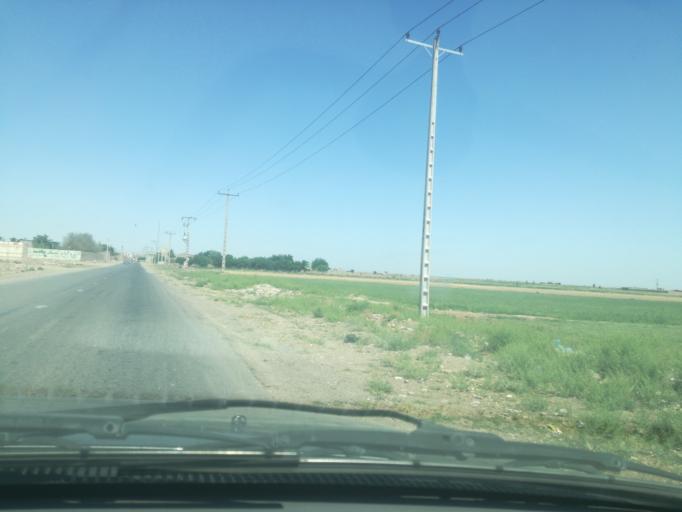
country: IR
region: Razavi Khorasan
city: Sarakhs
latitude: 36.5677
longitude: 61.1397
